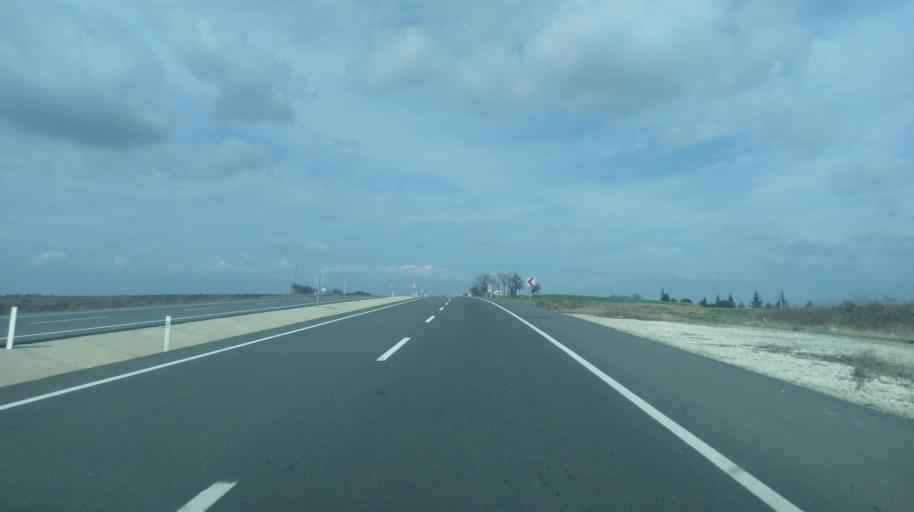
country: TR
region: Edirne
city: Hamidiye
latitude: 41.0601
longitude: 26.6408
